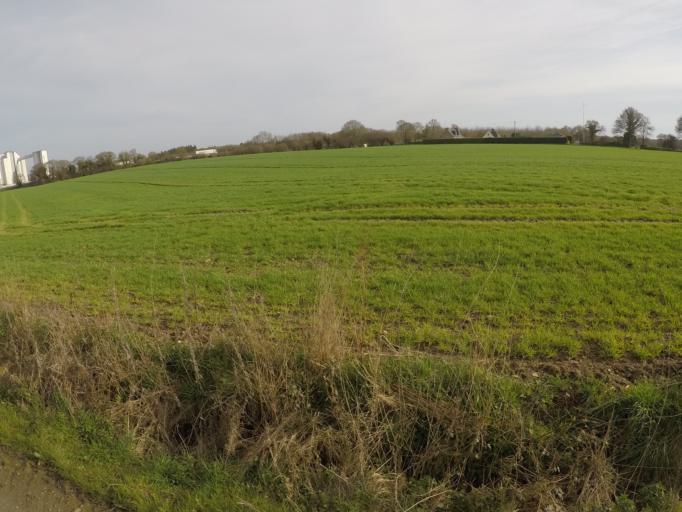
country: FR
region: Brittany
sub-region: Departement des Cotes-d'Armor
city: Plelo
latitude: 48.5272
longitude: -2.9625
